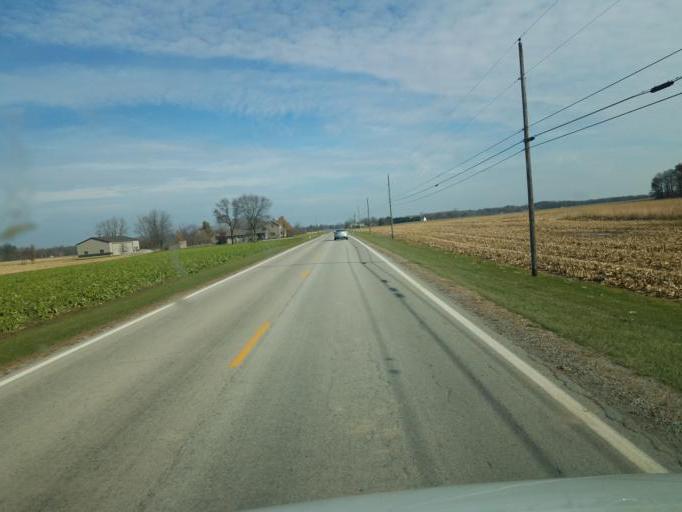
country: US
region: Ohio
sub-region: Hardin County
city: Forest
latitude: 40.7036
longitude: -83.4545
